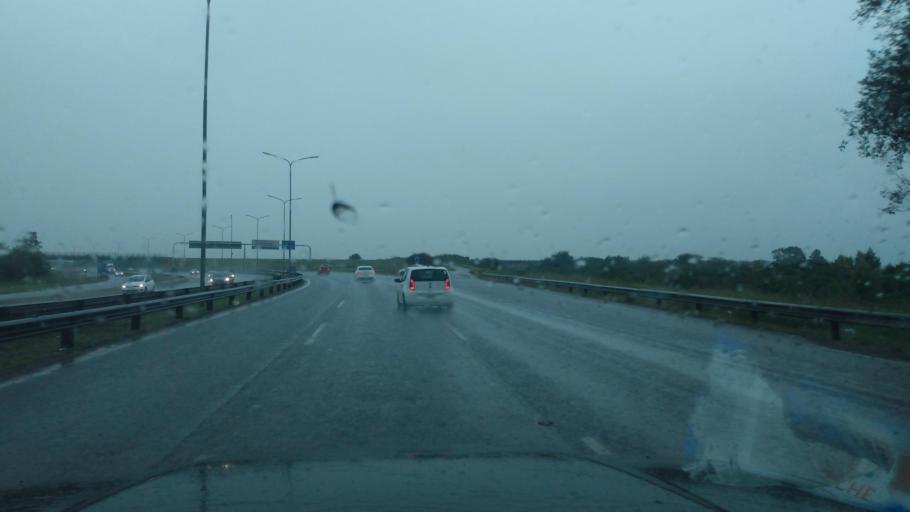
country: AR
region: Buenos Aires
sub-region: Partido de Tigre
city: Tigre
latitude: -34.4936
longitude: -58.5955
